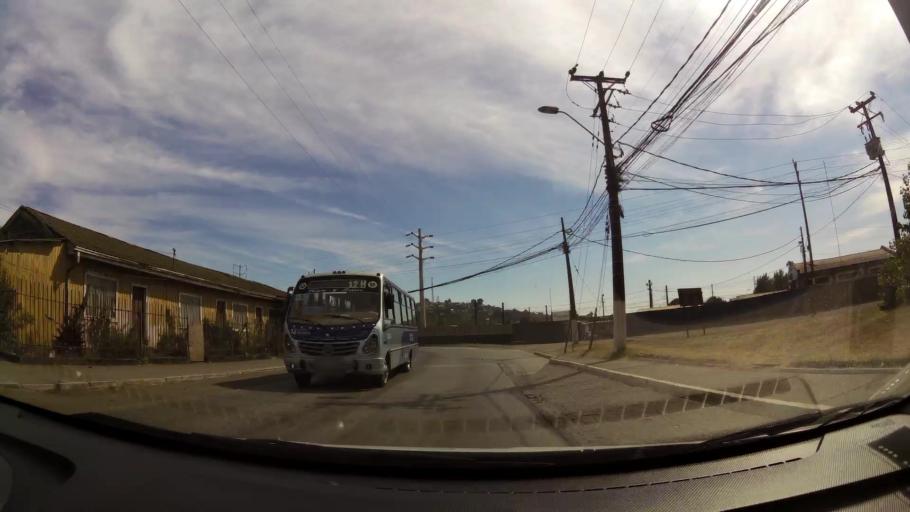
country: CL
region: Biobio
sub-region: Provincia de Concepcion
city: Talcahuano
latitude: -36.7269
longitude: -73.1168
